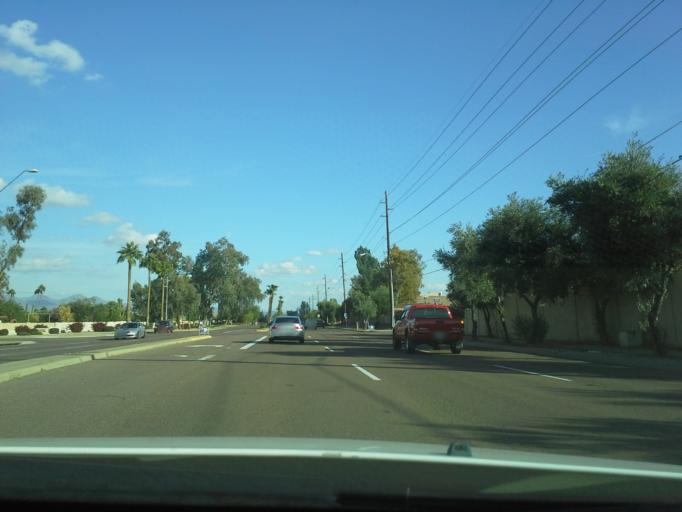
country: US
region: Arizona
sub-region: Maricopa County
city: Paradise Valley
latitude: 33.5826
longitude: -111.9873
